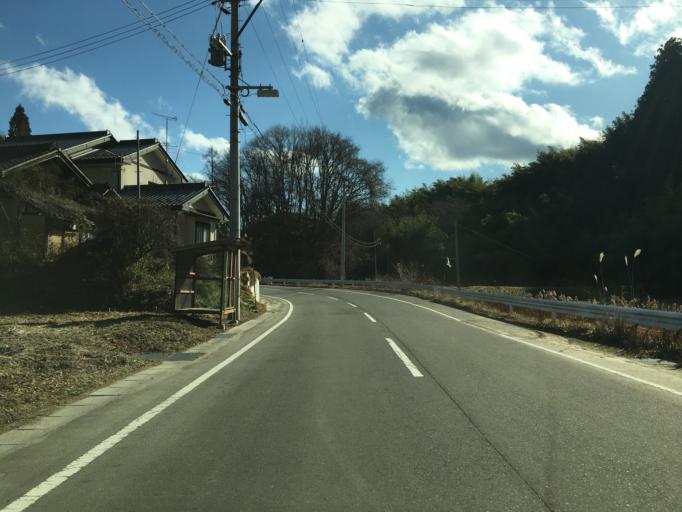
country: JP
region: Fukushima
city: Funehikimachi-funehiki
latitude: 37.4171
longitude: 140.5562
